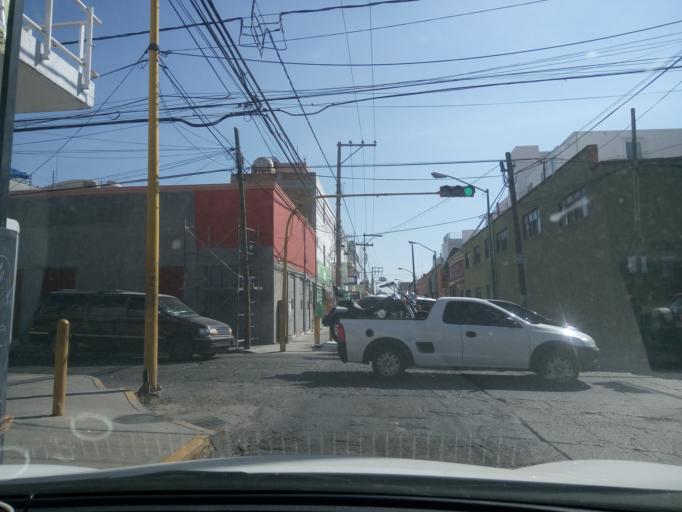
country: MX
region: Guanajuato
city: Leon
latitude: 21.1269
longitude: -101.6819
